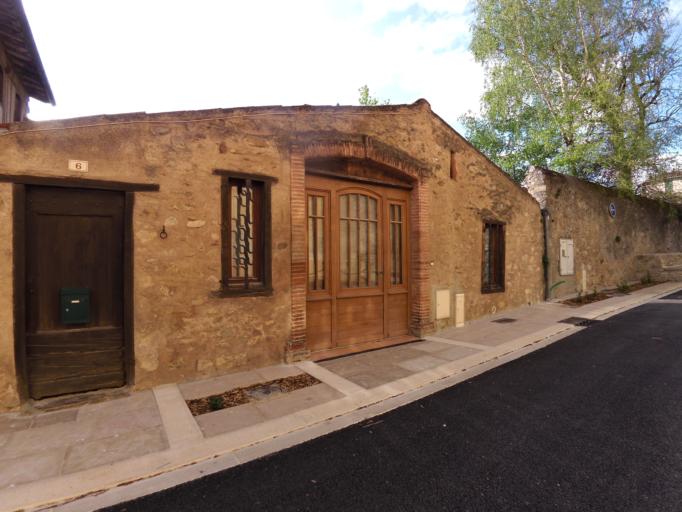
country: FR
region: Midi-Pyrenees
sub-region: Departement du Tarn
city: Soreze
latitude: 43.4520
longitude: 2.0671
